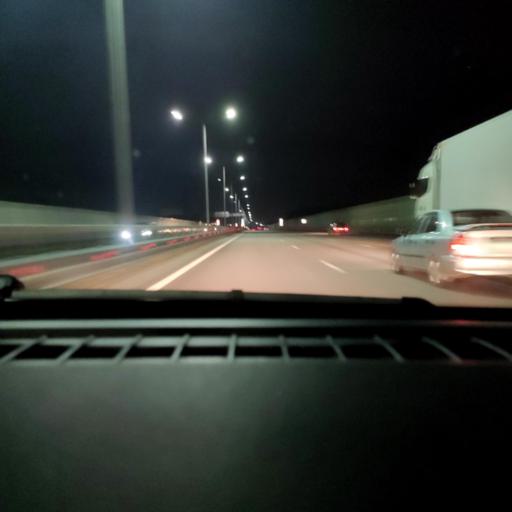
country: RU
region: Voronezj
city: Ramon'
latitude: 51.8202
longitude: 39.2510
